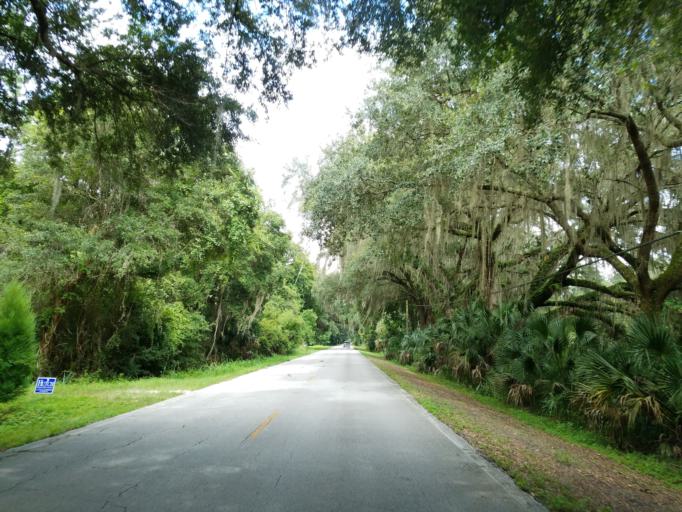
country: US
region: Florida
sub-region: Alachua County
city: Gainesville
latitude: 29.5025
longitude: -82.2716
